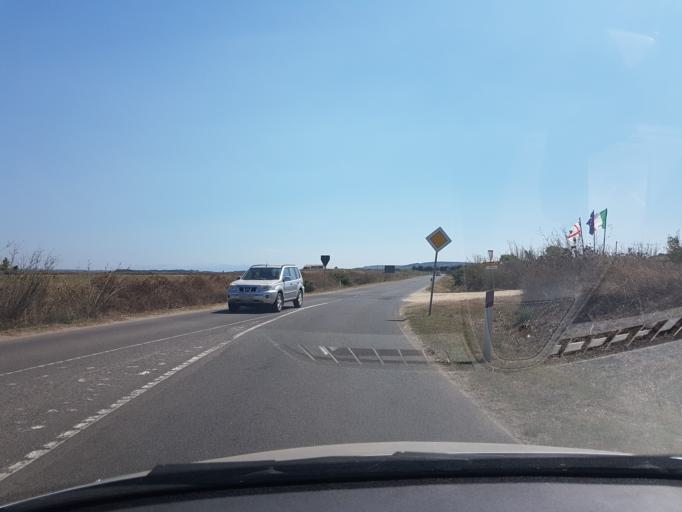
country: IT
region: Sardinia
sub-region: Provincia di Oristano
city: Nurachi
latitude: 39.9842
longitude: 8.4548
